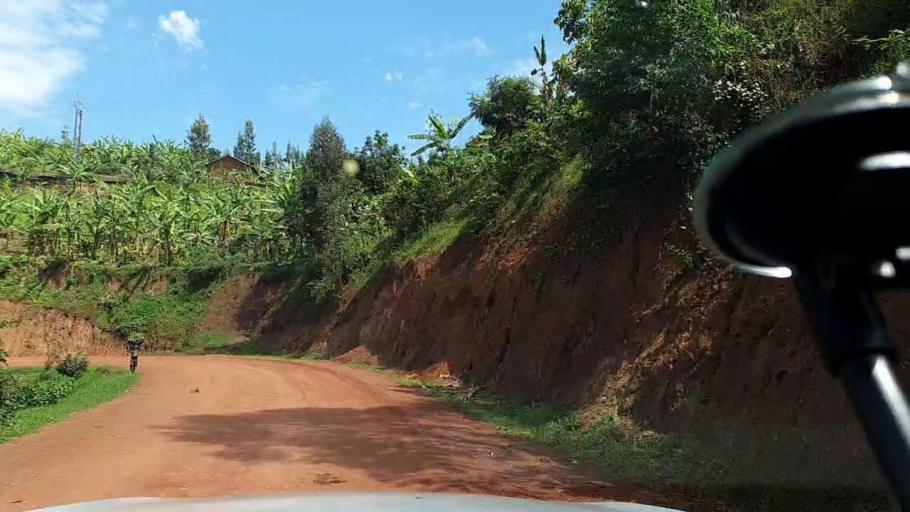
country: RW
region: Kigali
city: Kigali
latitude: -1.8013
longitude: 29.8939
